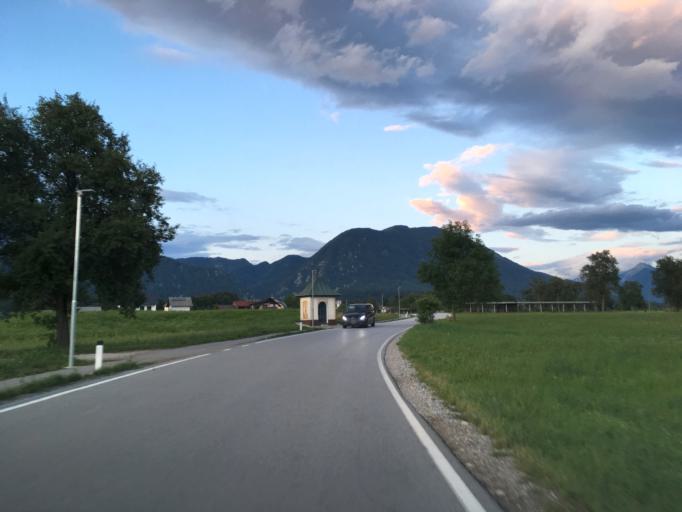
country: SI
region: Radovljica
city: Lesce
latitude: 46.3642
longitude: 14.1712
